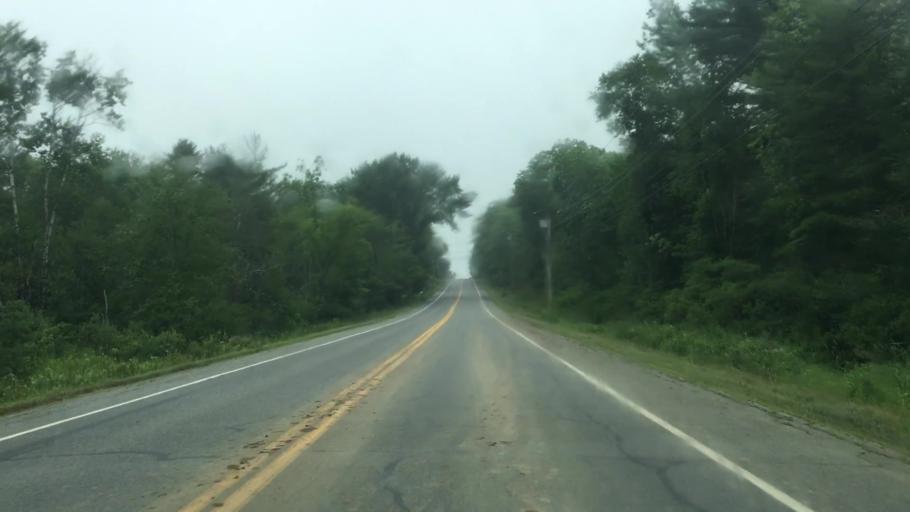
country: US
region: Maine
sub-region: Lincoln County
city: Wiscasset
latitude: 44.0628
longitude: -69.6892
